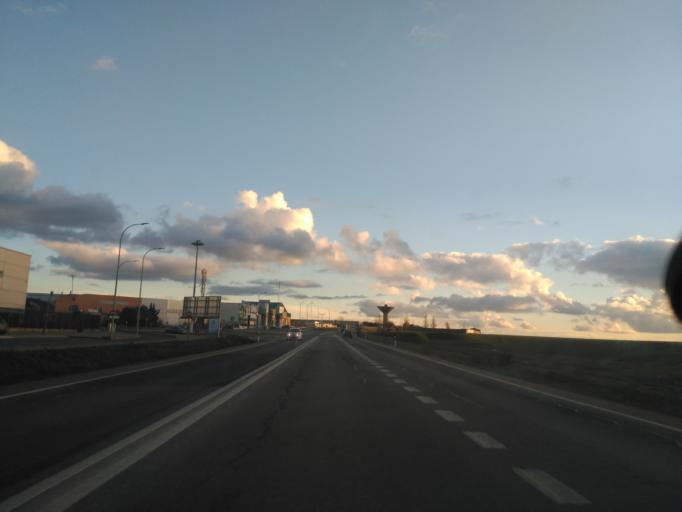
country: ES
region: Castille and Leon
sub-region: Provincia de Salamanca
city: Carbajosa de la Sagrada
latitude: 40.9384
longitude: -5.6685
